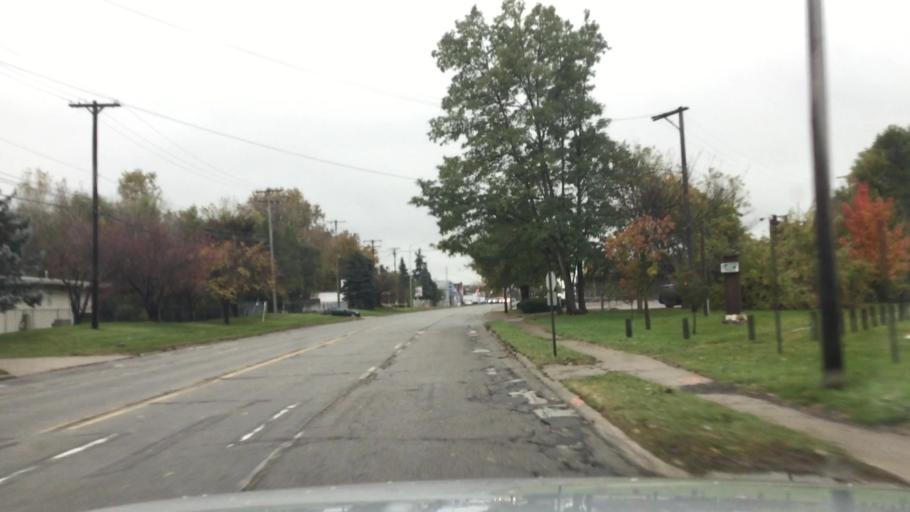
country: US
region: Michigan
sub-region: Oakland County
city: Sylvan Lake
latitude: 42.6238
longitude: -83.3161
